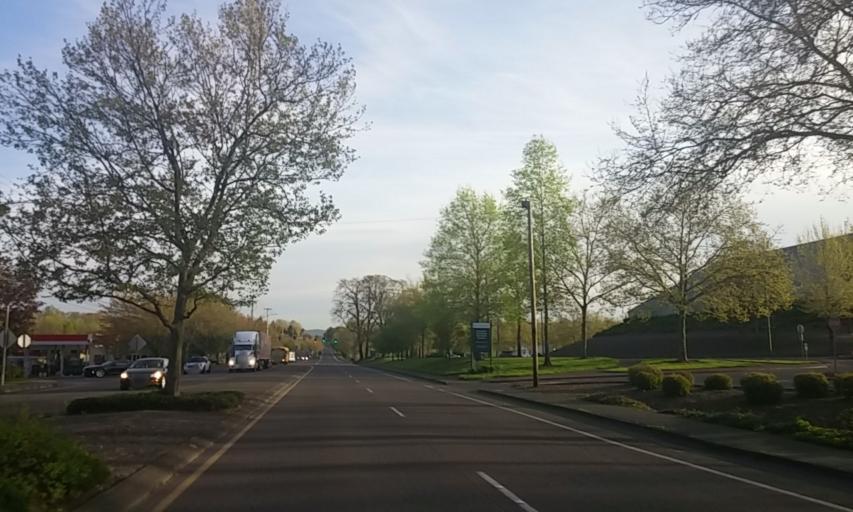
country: US
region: Oregon
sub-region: Washington County
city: Oak Hills
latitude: 45.5181
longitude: -122.8396
